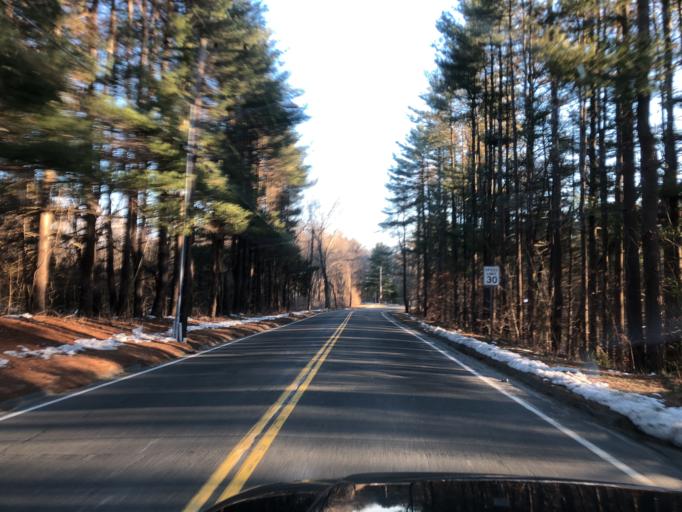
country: US
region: Connecticut
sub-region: Hartford County
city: Farmington
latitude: 41.7622
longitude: -72.8578
